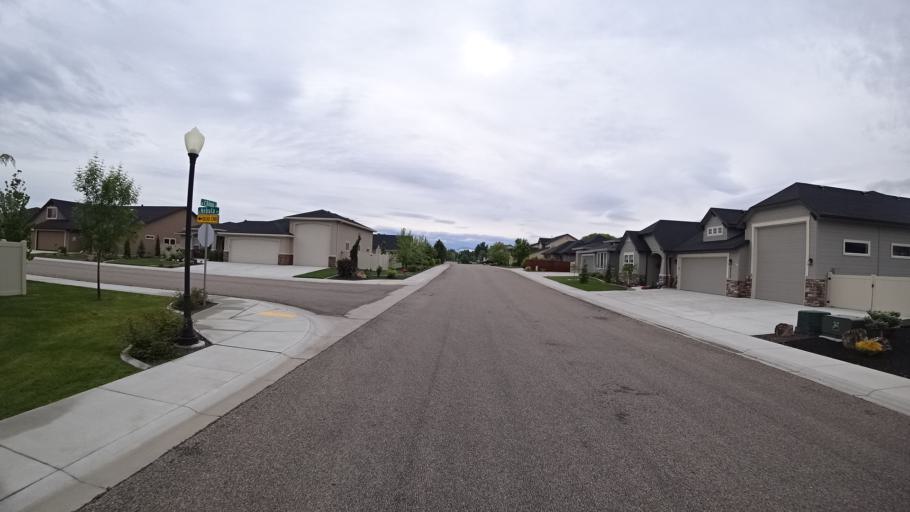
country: US
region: Idaho
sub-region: Ada County
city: Star
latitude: 43.6997
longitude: -116.4840
